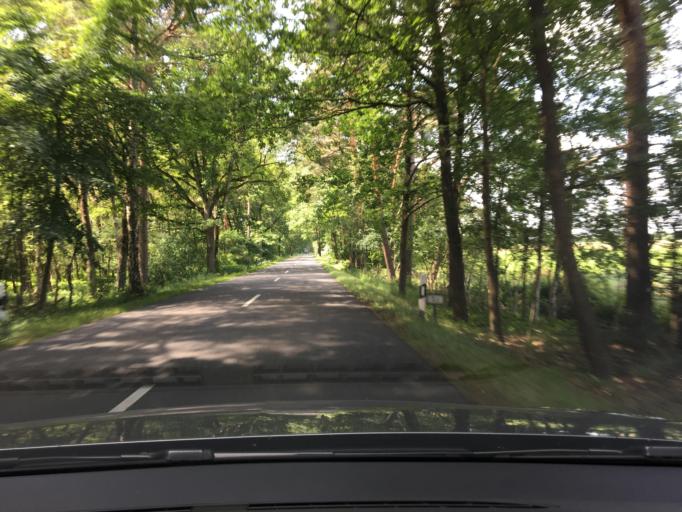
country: DE
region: Lower Saxony
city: Kirchtimke
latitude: 53.2497
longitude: 9.1979
